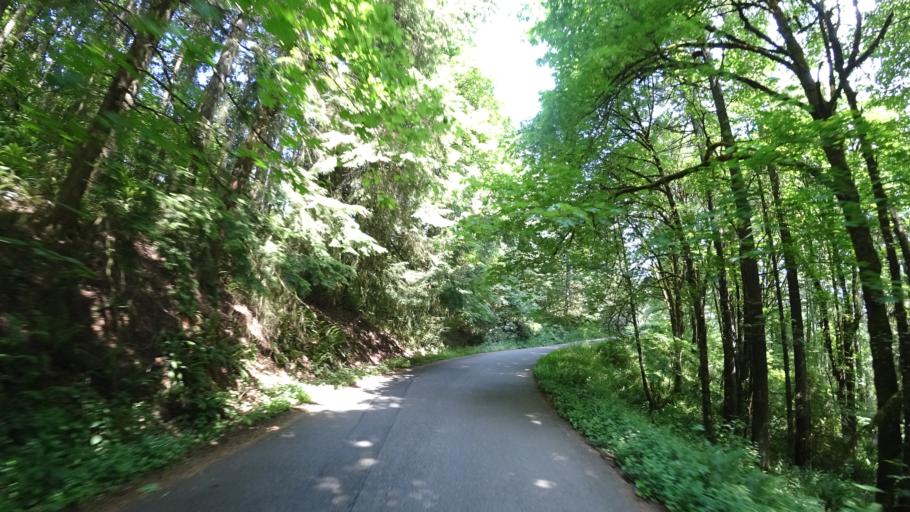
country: US
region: Oregon
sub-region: Multnomah County
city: Portland
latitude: 45.5201
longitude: -122.7188
